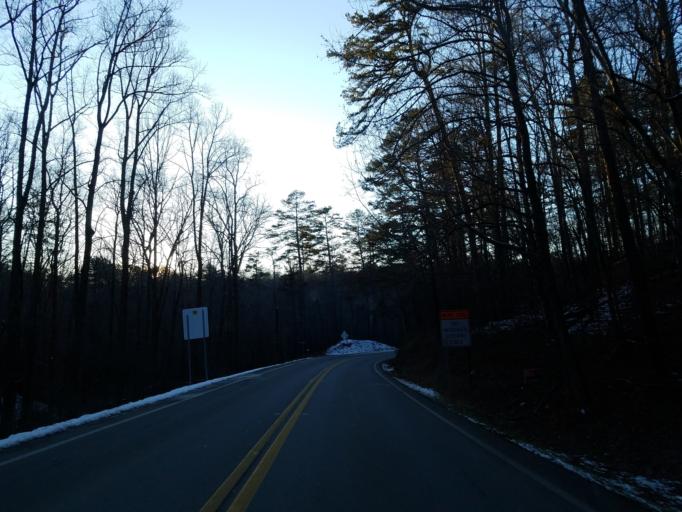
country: US
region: Georgia
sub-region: Dawson County
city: Dawsonville
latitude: 34.4250
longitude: -84.1663
